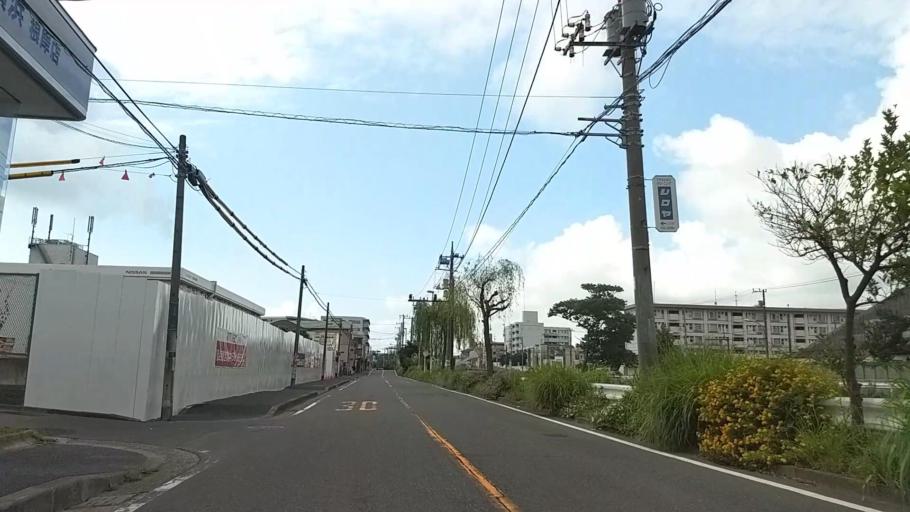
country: JP
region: Kanagawa
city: Yokohama
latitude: 35.4209
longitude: 139.6257
